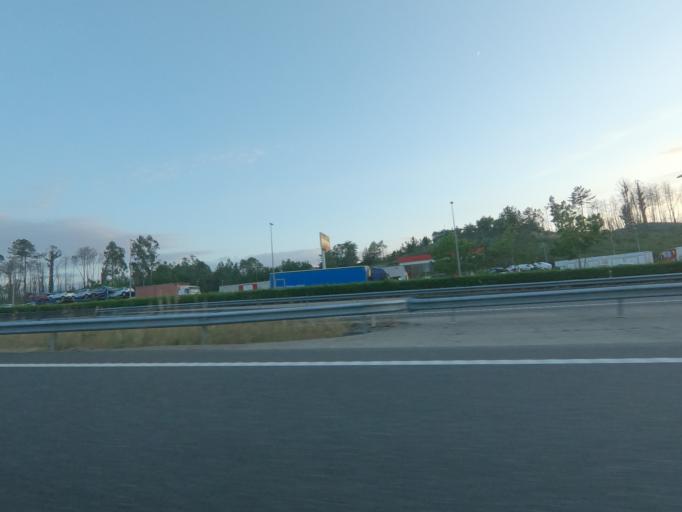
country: ES
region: Galicia
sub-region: Provincia de Pontevedra
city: Ponteareas
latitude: 42.1461
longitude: -8.4757
